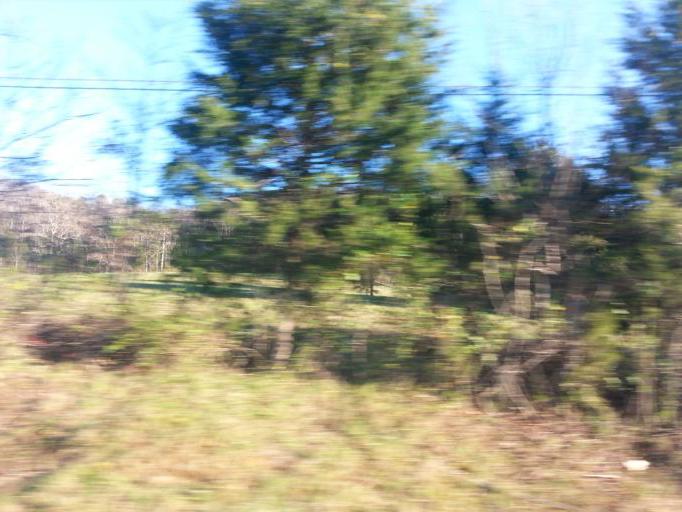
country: US
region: Tennessee
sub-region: Anderson County
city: Rocky Top
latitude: 36.1552
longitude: -84.1716
